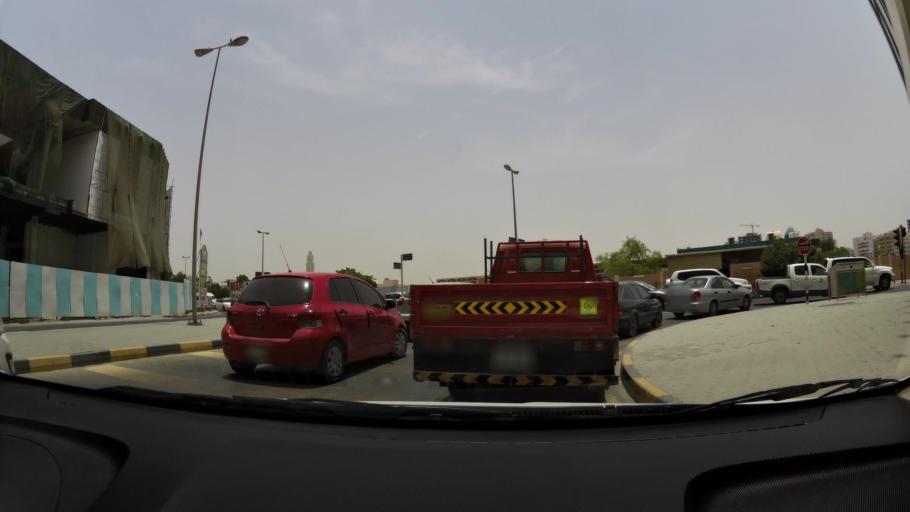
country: AE
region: Ash Shariqah
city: Sharjah
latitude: 25.3541
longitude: 55.3948
